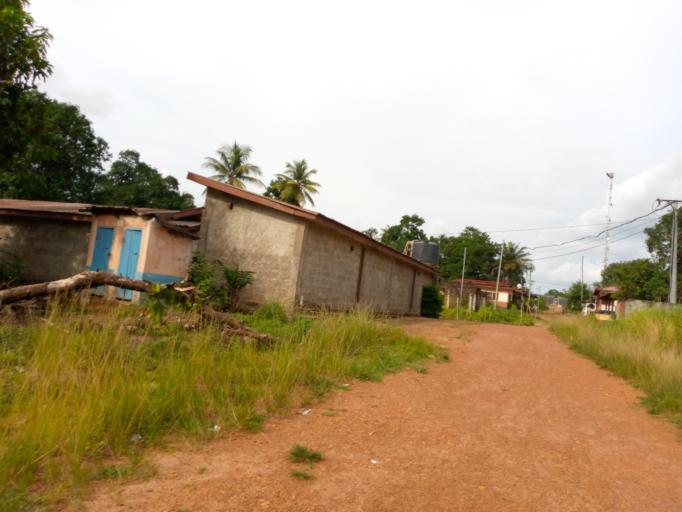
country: SL
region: Northern Province
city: Magburaka
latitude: 8.7173
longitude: -11.9513
